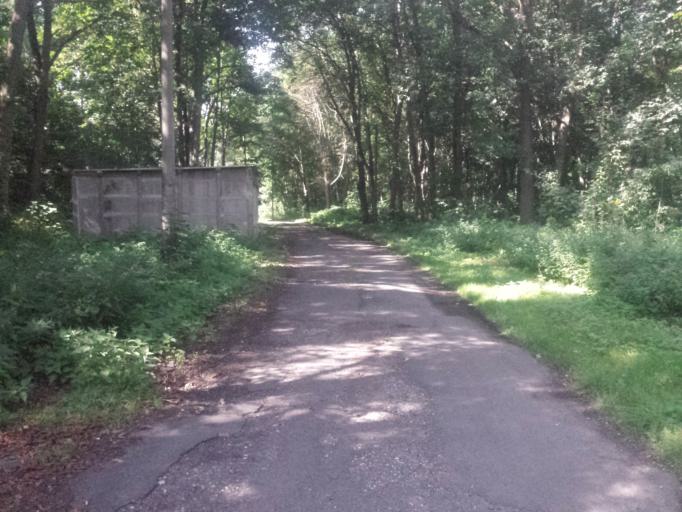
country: DE
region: Saxony
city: Taucha
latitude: 51.3908
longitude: 12.4725
